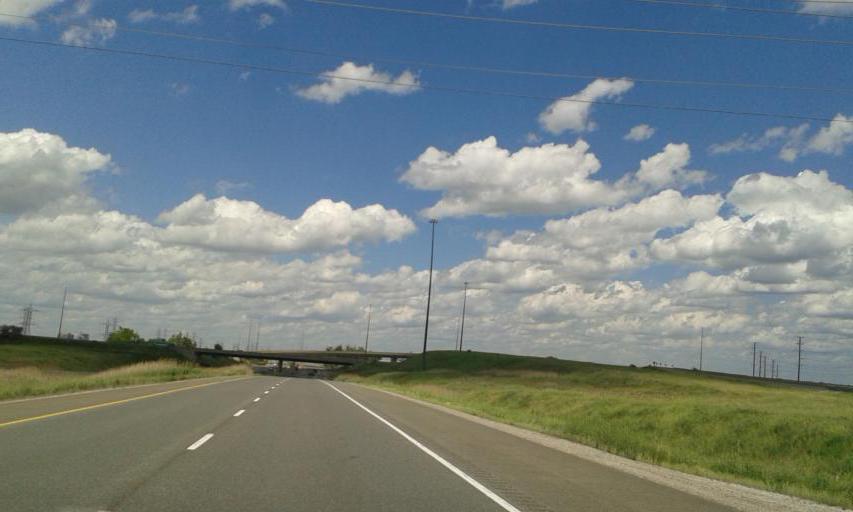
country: CA
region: Ontario
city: Oakville
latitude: 43.5235
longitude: -79.7299
